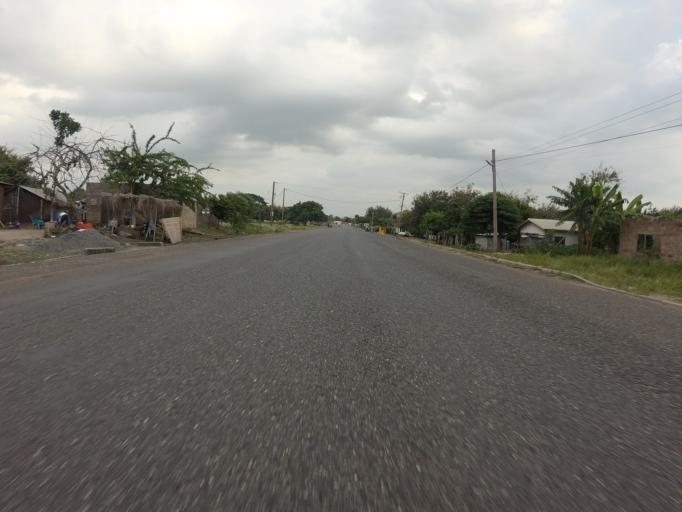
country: GH
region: Volta
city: Ho
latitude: 6.4914
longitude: 0.4877
